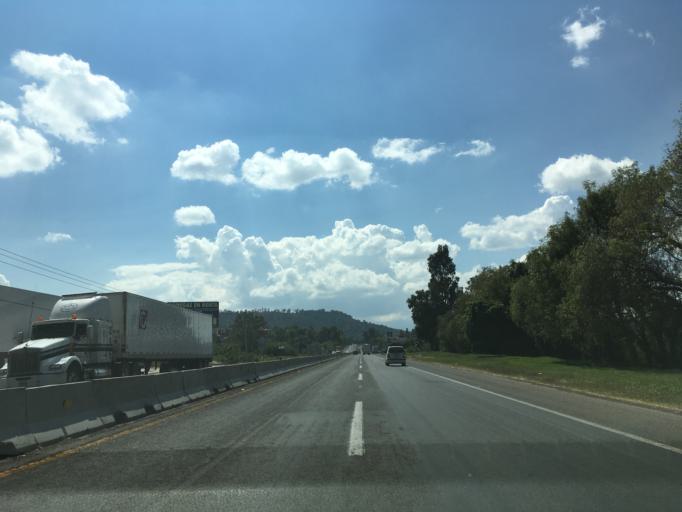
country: MX
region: Michoacan
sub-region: Morelia
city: Morelos
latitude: 19.6574
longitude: -101.2417
